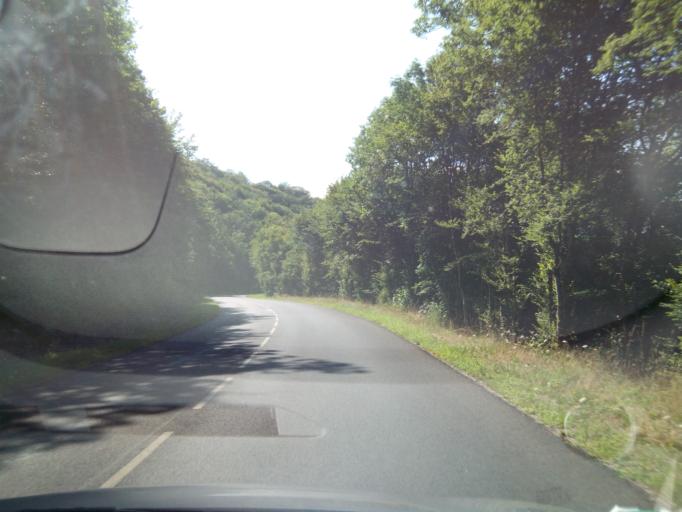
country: FR
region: Limousin
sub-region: Departement de la Correze
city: Beynat
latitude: 45.1238
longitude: 1.6930
